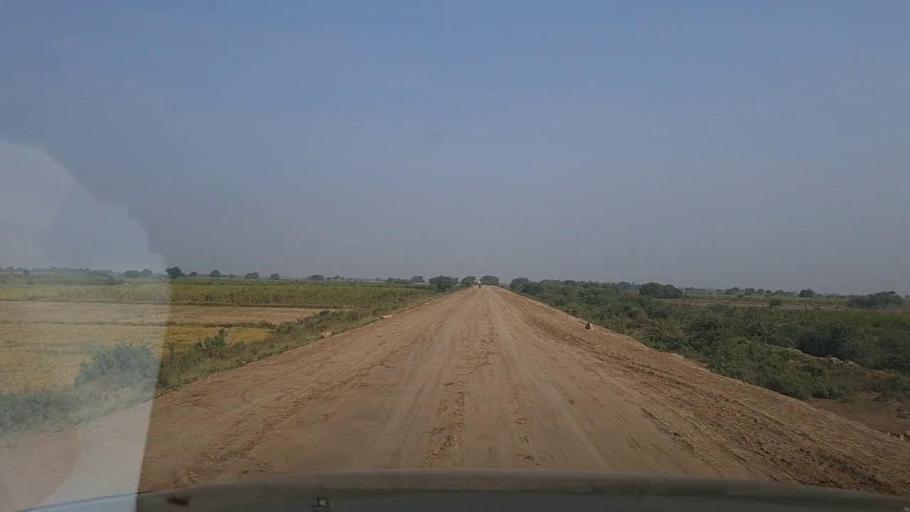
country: PK
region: Sindh
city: Bulri
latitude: 24.9829
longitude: 68.2938
